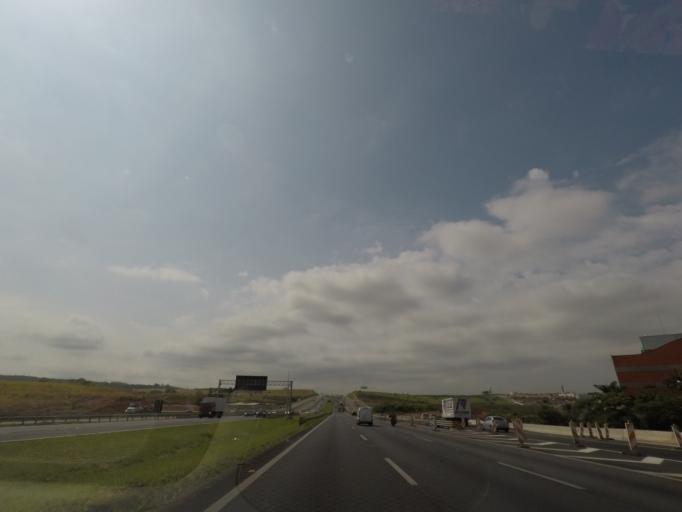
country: BR
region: Sao Paulo
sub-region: Campinas
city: Campinas
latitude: -22.8651
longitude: -47.0209
